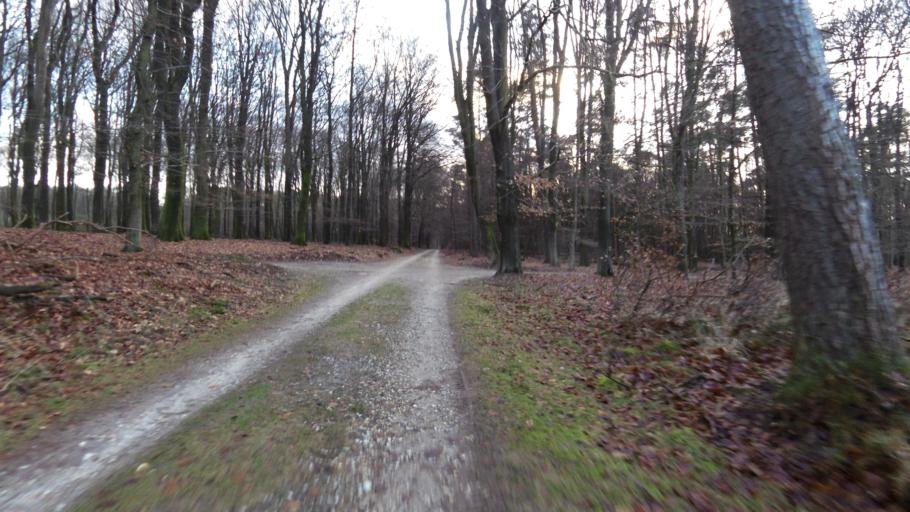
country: NL
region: Gelderland
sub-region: Gemeente Epe
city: Vaassen
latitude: 52.3127
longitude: 5.8692
